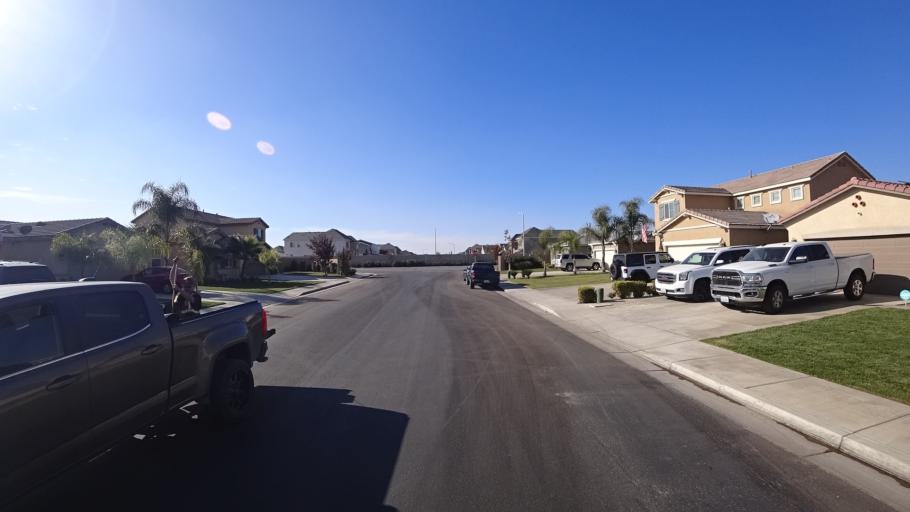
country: US
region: California
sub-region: Kern County
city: Greenfield
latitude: 35.2927
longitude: -119.0648
